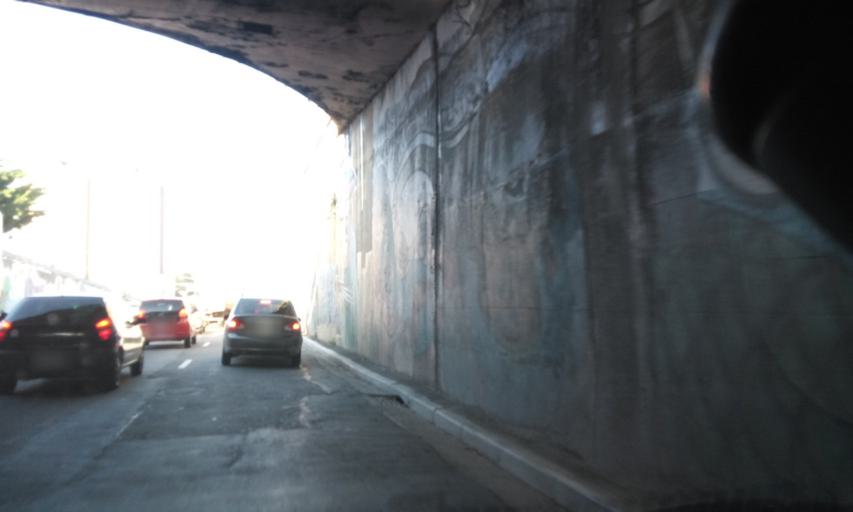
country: BR
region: Sao Paulo
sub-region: Santo Andre
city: Santo Andre
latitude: -23.6647
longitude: -46.5155
